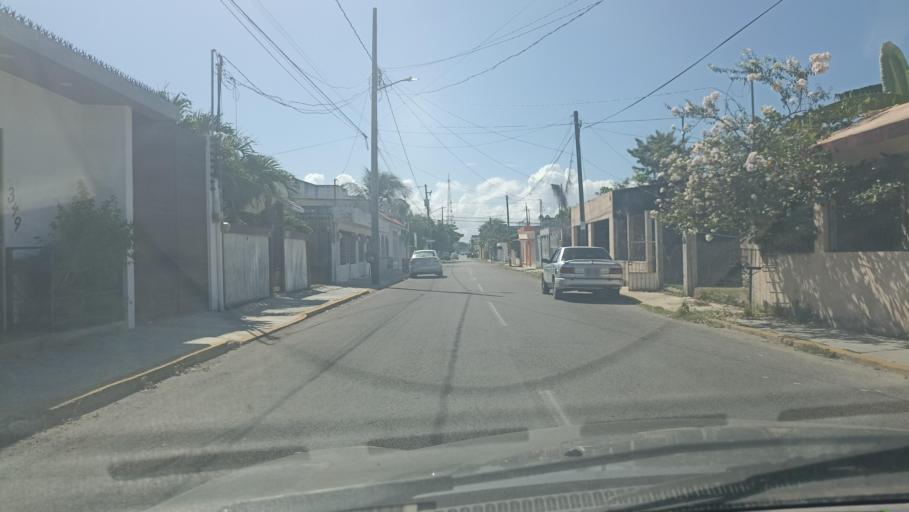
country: MX
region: Quintana Roo
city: Chetumal
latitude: 18.5112
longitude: -88.2883
